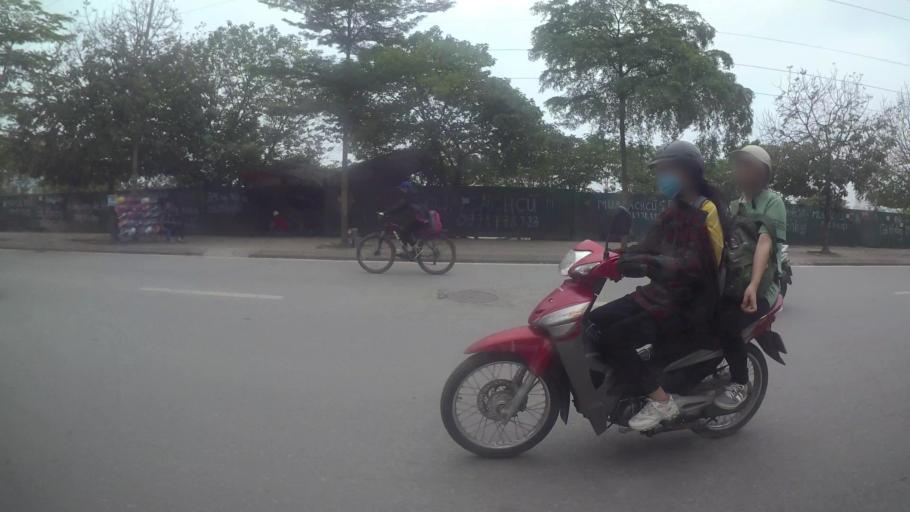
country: VN
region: Ha Noi
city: Cau Dien
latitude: 21.0248
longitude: 105.7784
